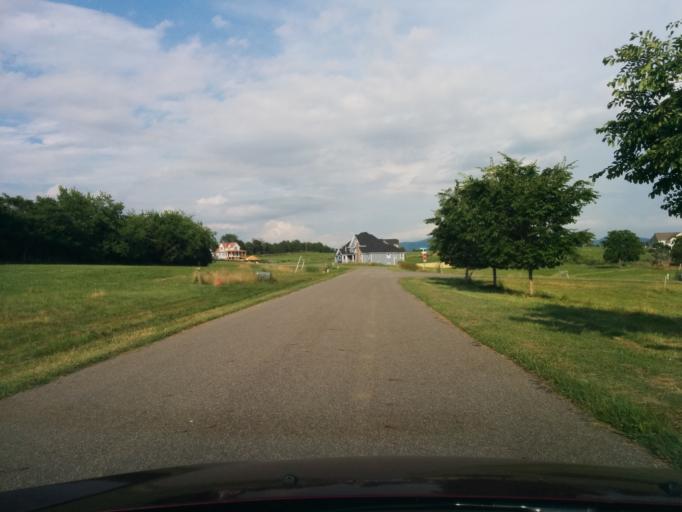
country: US
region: Virginia
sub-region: Rockbridge County
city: East Lexington
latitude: 37.7941
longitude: -79.4084
